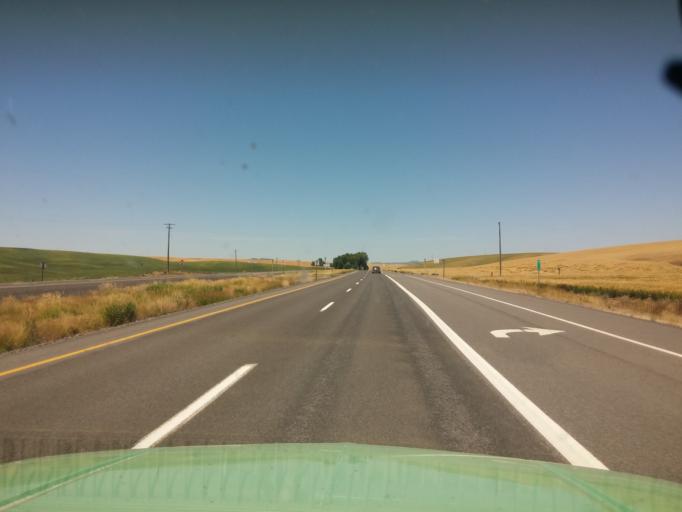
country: US
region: Idaho
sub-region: Nez Perce County
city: Lewiston
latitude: 46.5627
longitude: -116.9488
